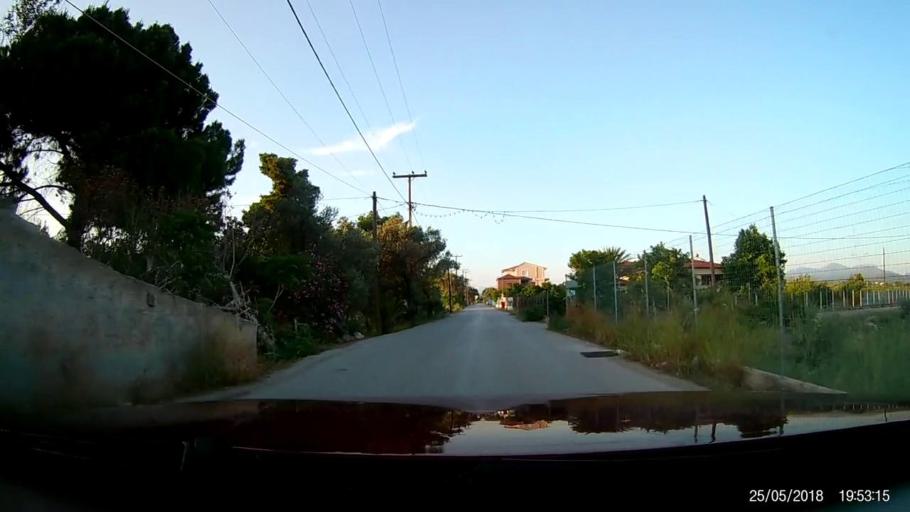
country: GR
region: Central Greece
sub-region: Nomos Evvoias
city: Ayios Nikolaos
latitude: 38.4158
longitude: 23.6497
